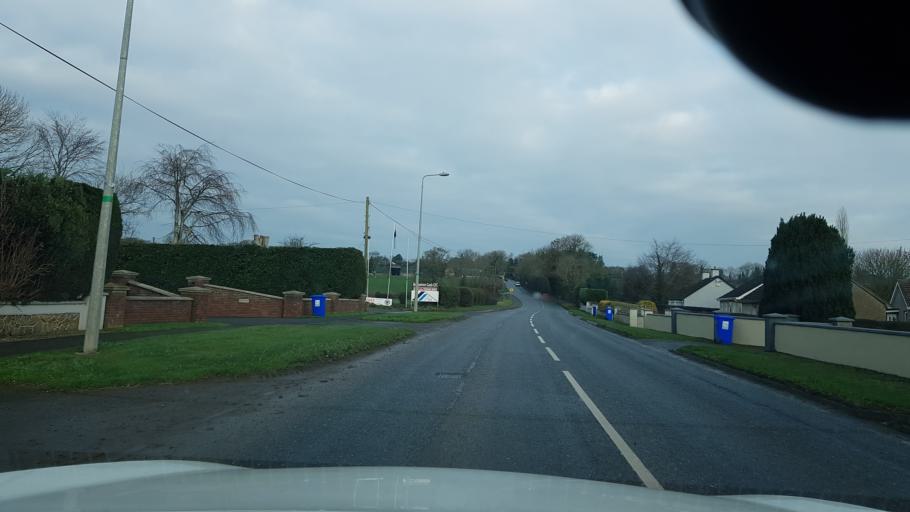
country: IE
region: Leinster
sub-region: An Mhi
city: Navan
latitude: 53.6732
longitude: -6.6775
